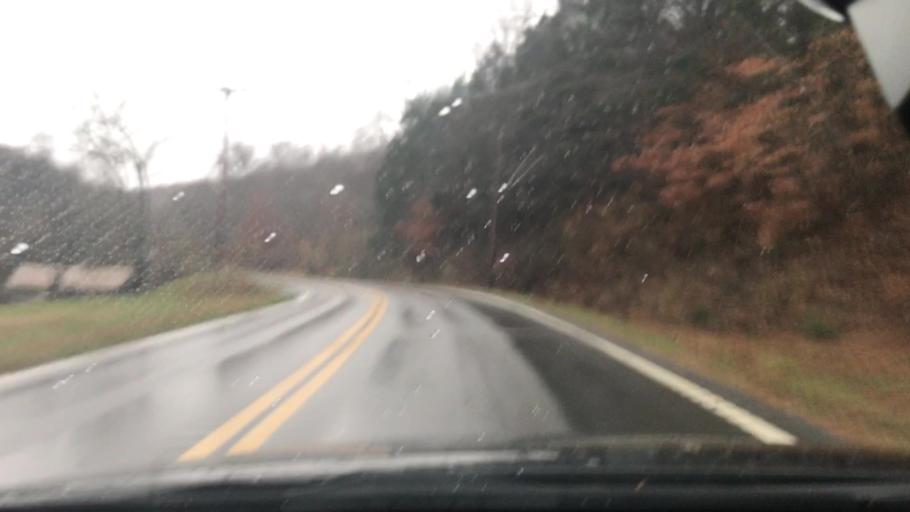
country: US
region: Tennessee
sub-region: Cheatham County
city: Ashland City
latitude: 36.2781
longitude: -87.1404
